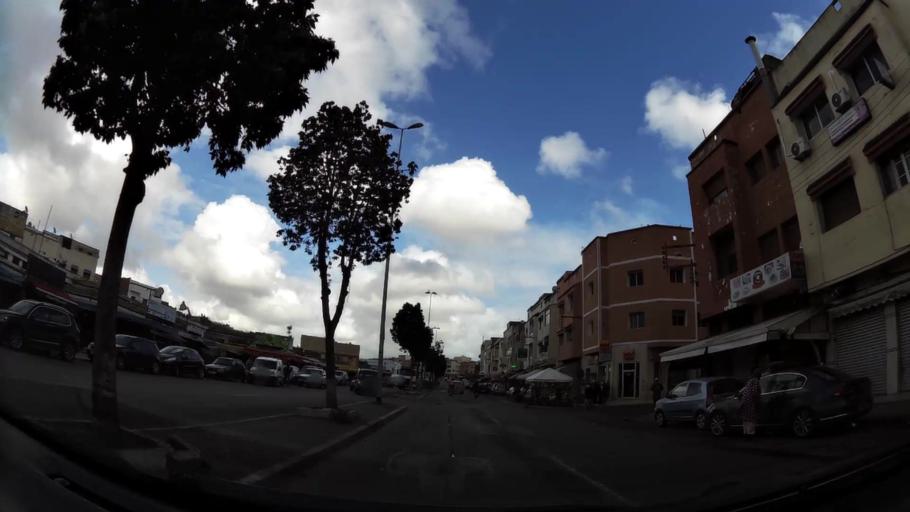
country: MA
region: Grand Casablanca
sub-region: Casablanca
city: Casablanca
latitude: 33.5476
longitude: -7.5983
